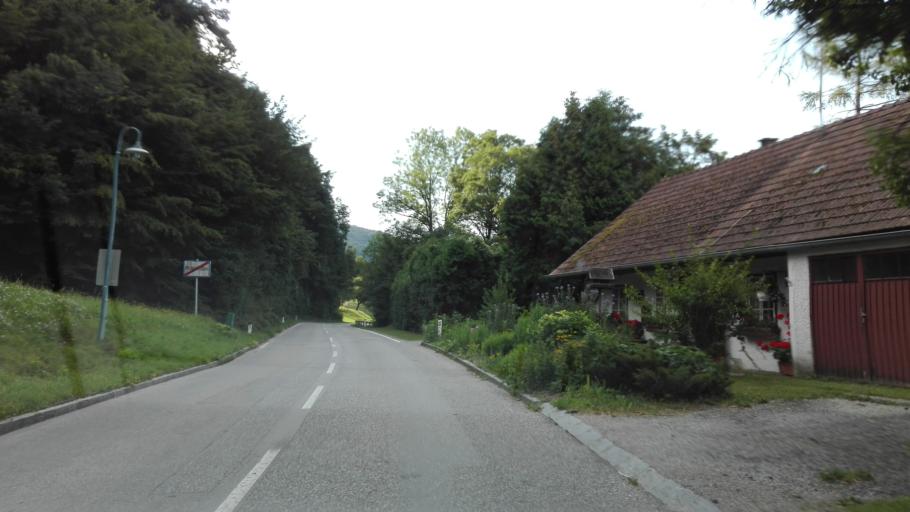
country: AT
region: Lower Austria
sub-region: Politischer Bezirk Sankt Polten
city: Kasten bei Boheimkirchen
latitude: 48.1144
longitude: 15.7555
